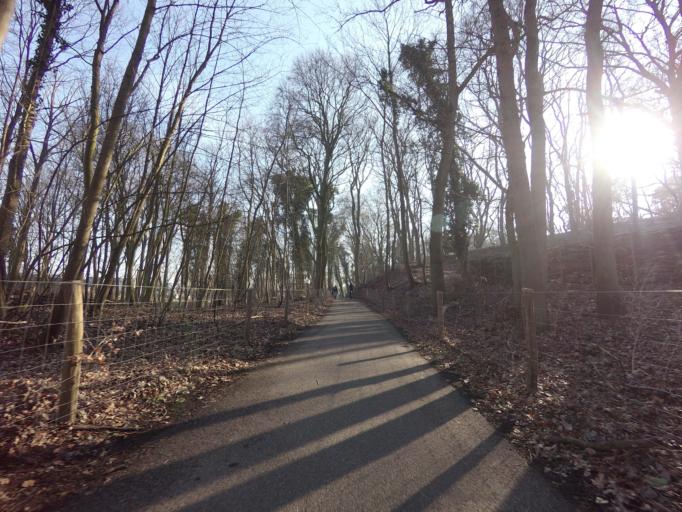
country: NL
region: North Holland
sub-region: Gemeente Bloemendaal
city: Bloemendaal
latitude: 52.4234
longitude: 4.6167
